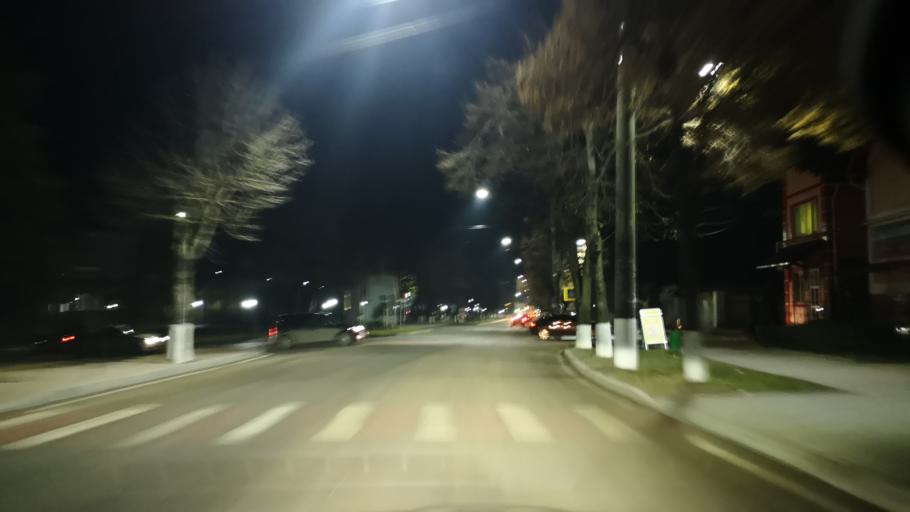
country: MD
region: Orhei
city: Orhei
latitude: 47.3823
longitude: 28.8253
